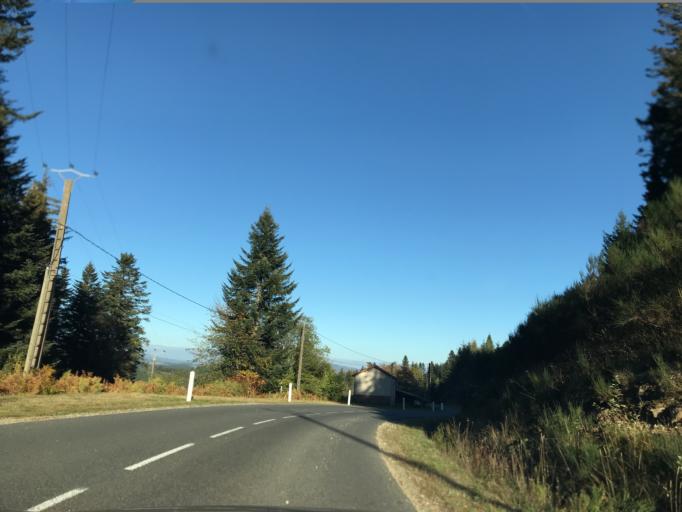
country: FR
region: Rhone-Alpes
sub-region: Departement de la Loire
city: Noiretable
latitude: 45.8063
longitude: 3.7192
